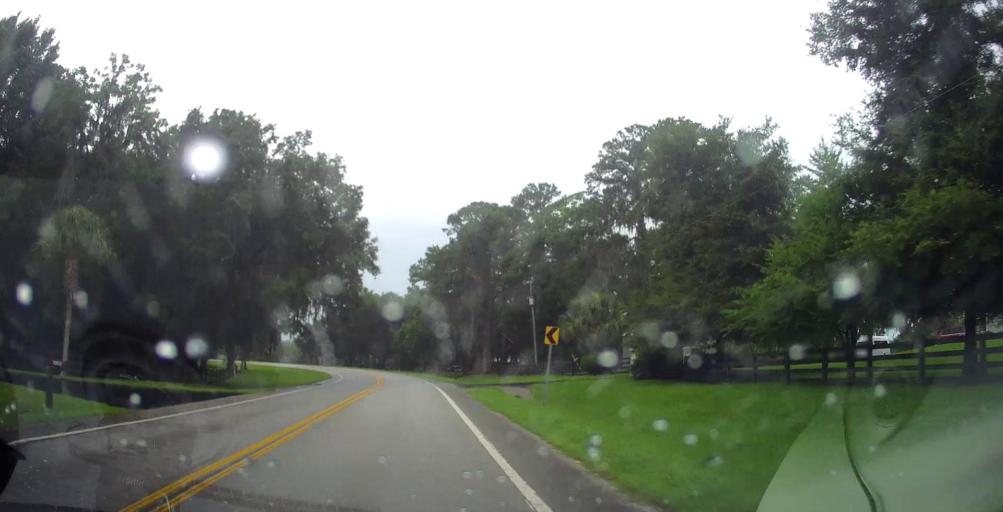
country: US
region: Florida
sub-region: Marion County
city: Citra
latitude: 29.3871
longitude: -82.2507
